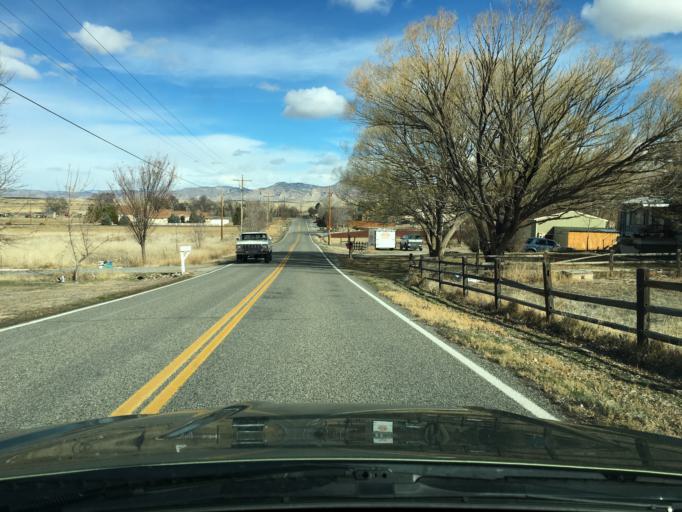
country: US
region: Colorado
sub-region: Mesa County
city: Grand Junction
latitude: 39.1324
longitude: -108.5616
